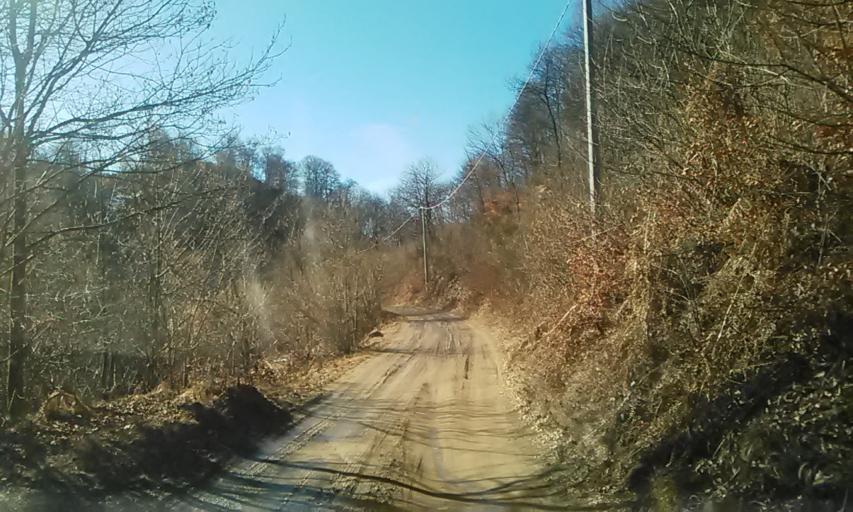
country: IT
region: Piedmont
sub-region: Provincia di Vercelli
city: Civiasco
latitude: 45.7921
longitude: 8.3007
